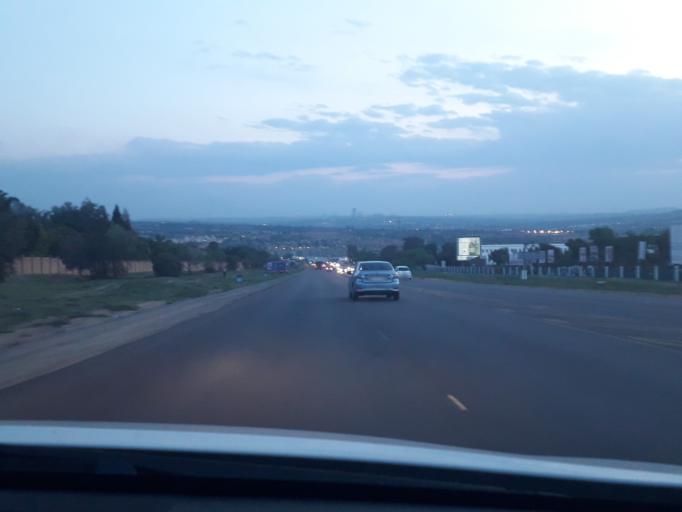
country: ZA
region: Gauteng
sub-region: City of Johannesburg Metropolitan Municipality
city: Midrand
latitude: -25.9916
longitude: 28.0767
